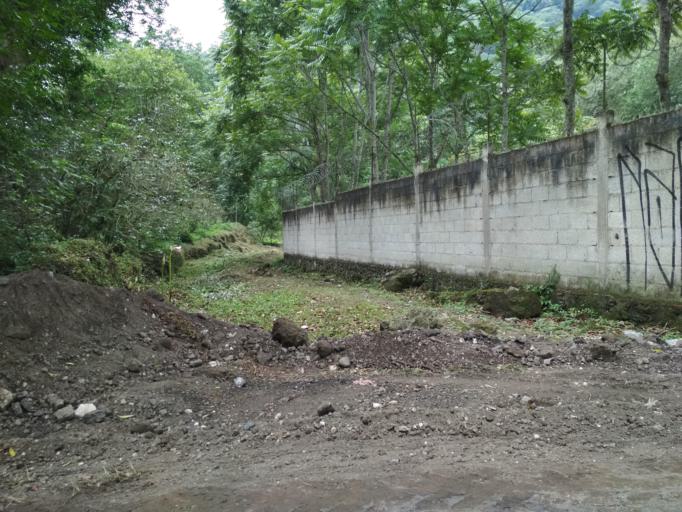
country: MX
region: Veracruz
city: Jilotepec
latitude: 19.6172
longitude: -96.9310
